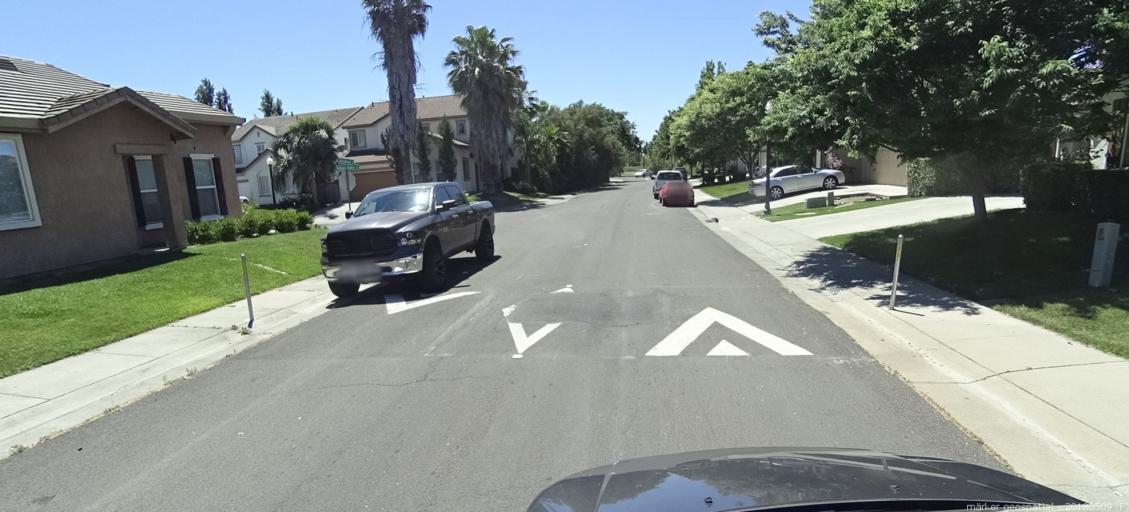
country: US
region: California
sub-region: Sacramento County
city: Sacramento
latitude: 38.6342
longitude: -121.5086
